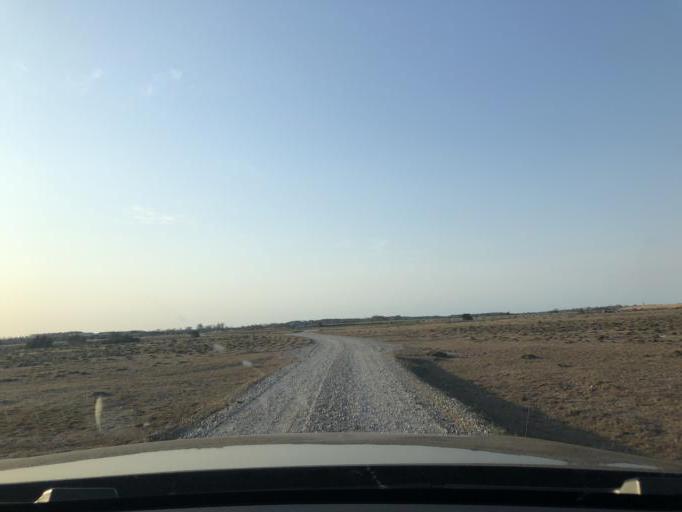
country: SE
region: Kalmar
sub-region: Morbylanga Kommun
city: Sodra Sandby
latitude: 56.5556
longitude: 16.6369
